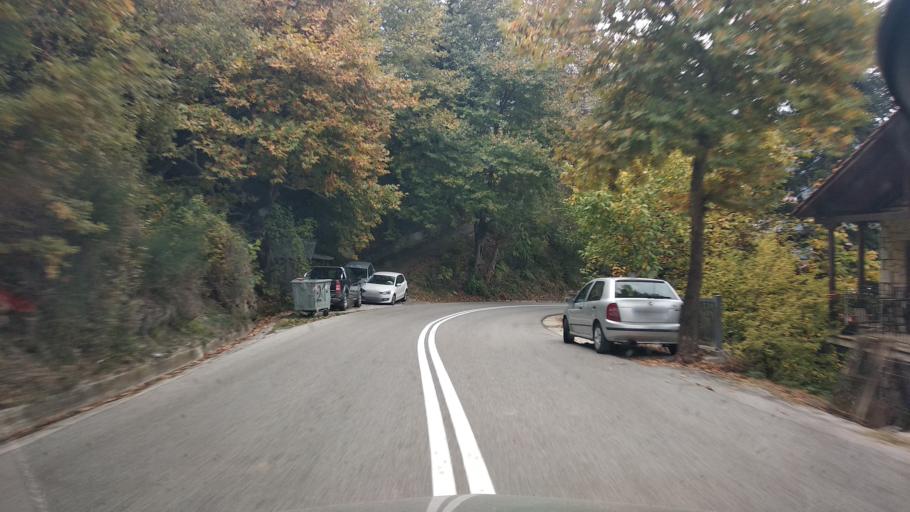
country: GR
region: Thessaly
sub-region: Trikala
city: Pyli
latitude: 39.5040
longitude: 21.5365
